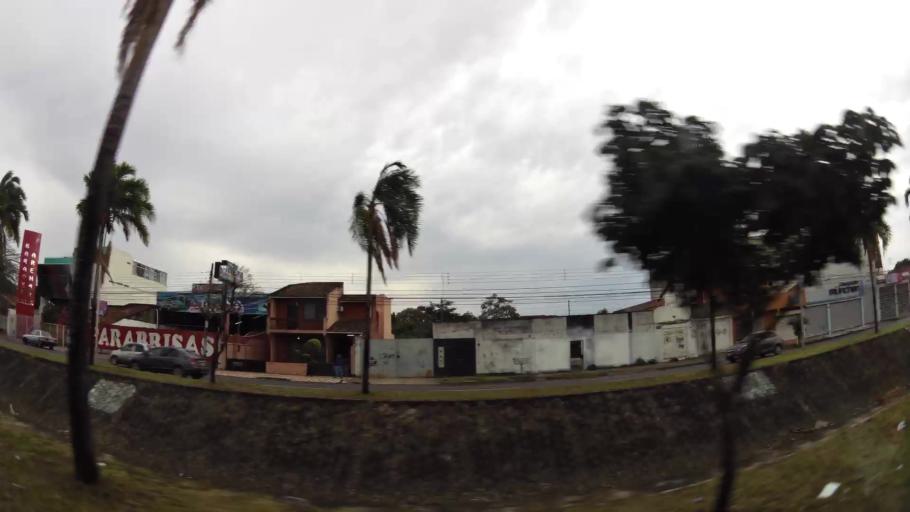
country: BO
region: Santa Cruz
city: Santa Cruz de la Sierra
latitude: -17.7820
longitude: -63.1613
